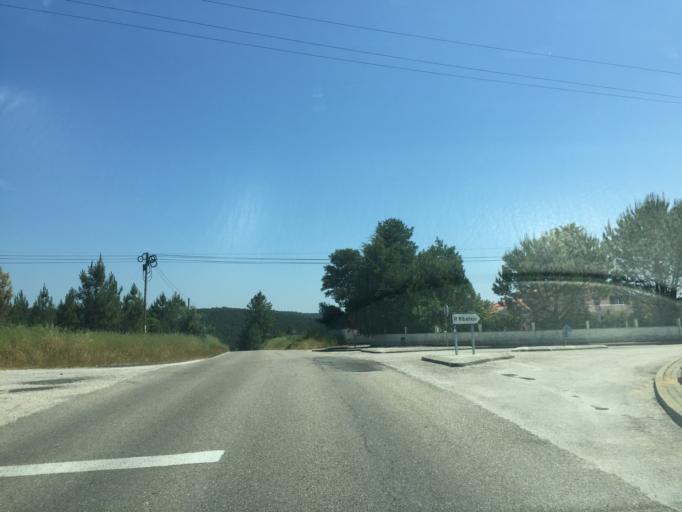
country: PT
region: Santarem
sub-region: Constancia
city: Constancia
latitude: 39.4707
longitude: -8.3479
